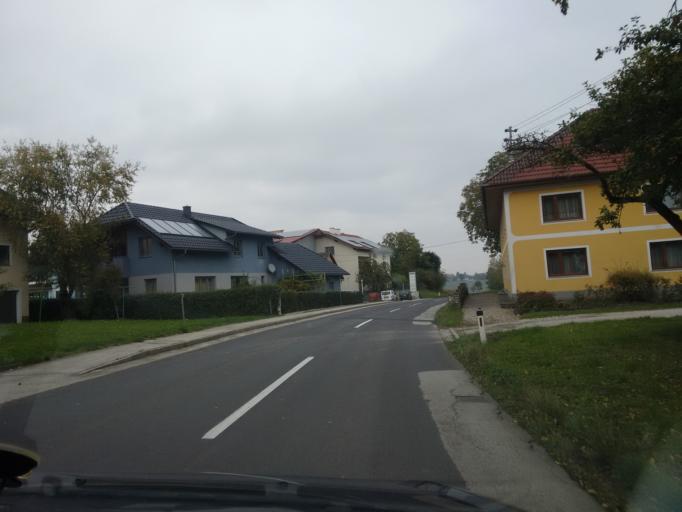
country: AT
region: Upper Austria
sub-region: Wels-Land
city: Sattledt
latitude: 48.0302
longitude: 14.0822
